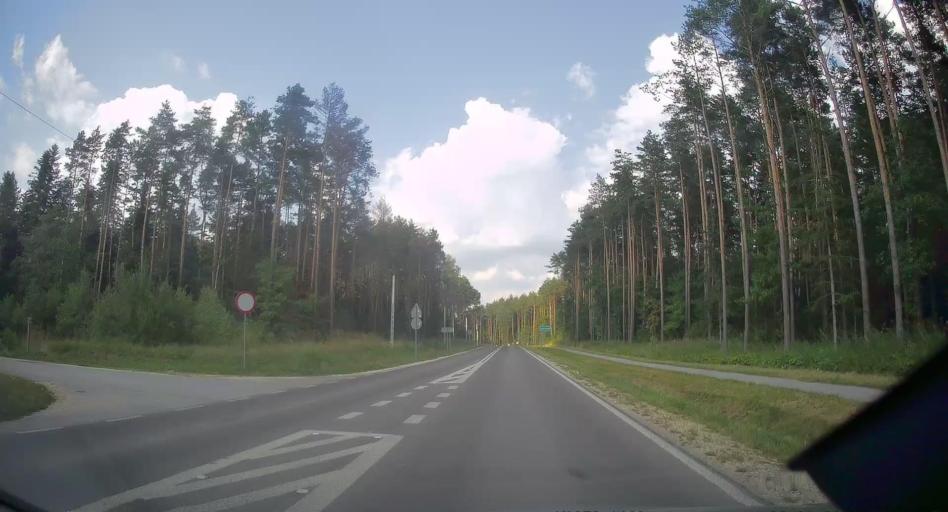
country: PL
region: Swietokrzyskie
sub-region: Powiat konecki
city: Radoszyce
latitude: 51.0182
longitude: 20.2891
